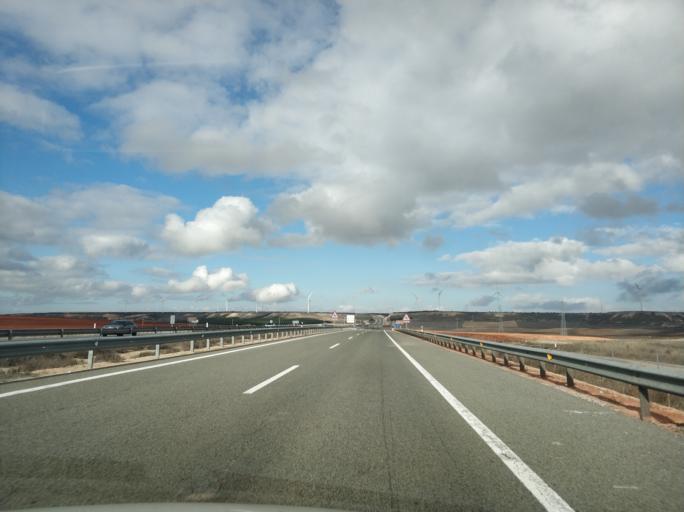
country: ES
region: Castille and Leon
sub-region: Provincia de Soria
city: Alcubilla de las Penas
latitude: 41.2681
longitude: -2.4742
